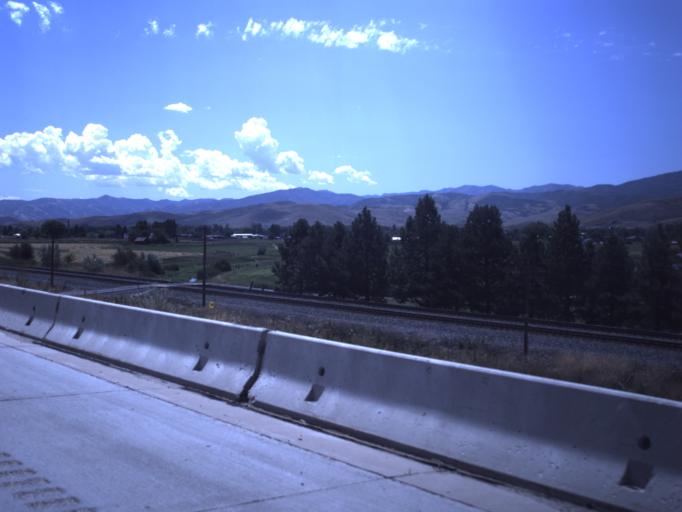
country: US
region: Utah
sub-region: Morgan County
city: Morgan
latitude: 41.0732
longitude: -111.7187
